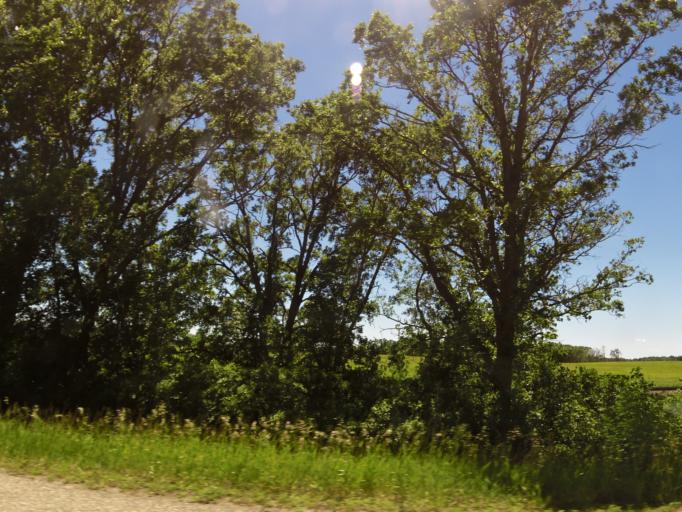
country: US
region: Minnesota
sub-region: Otter Tail County
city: New York Mills
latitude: 46.4744
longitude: -95.2770
